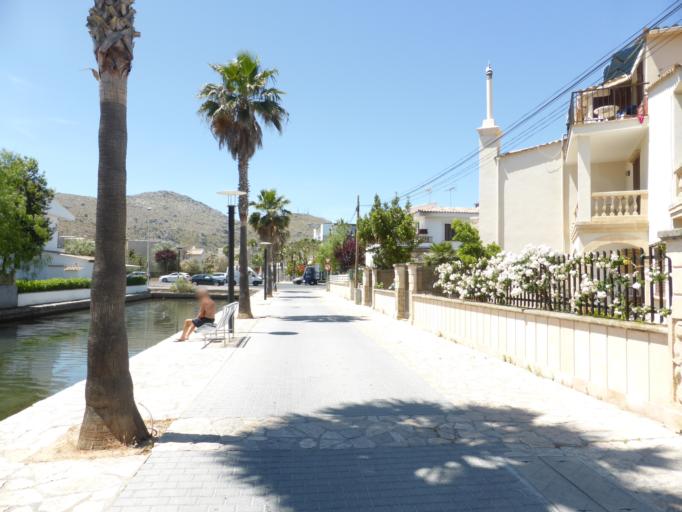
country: ES
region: Balearic Islands
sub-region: Illes Balears
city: Port d'Alcudia
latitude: 39.8304
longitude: 3.1174
